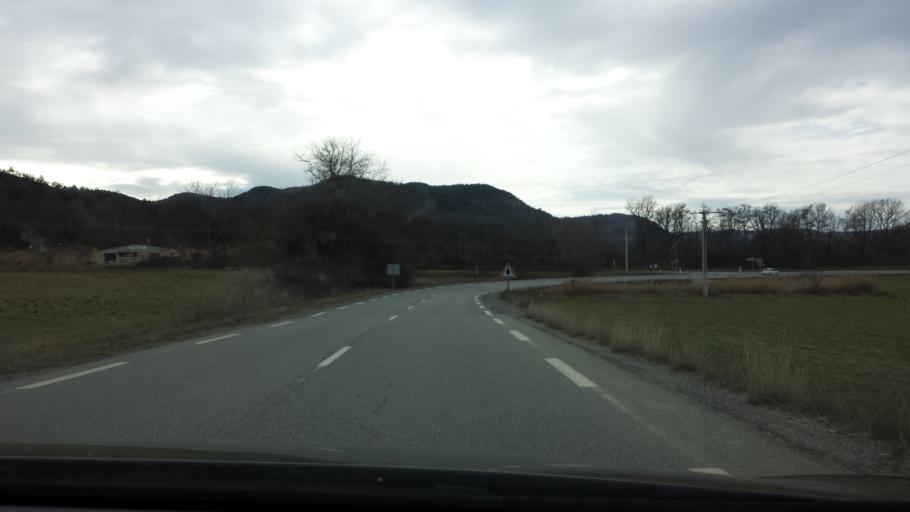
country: FR
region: Provence-Alpes-Cote d'Azur
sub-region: Departement des Alpes-de-Haute-Provence
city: Mallemoisson
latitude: 44.0384
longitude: 6.1483
